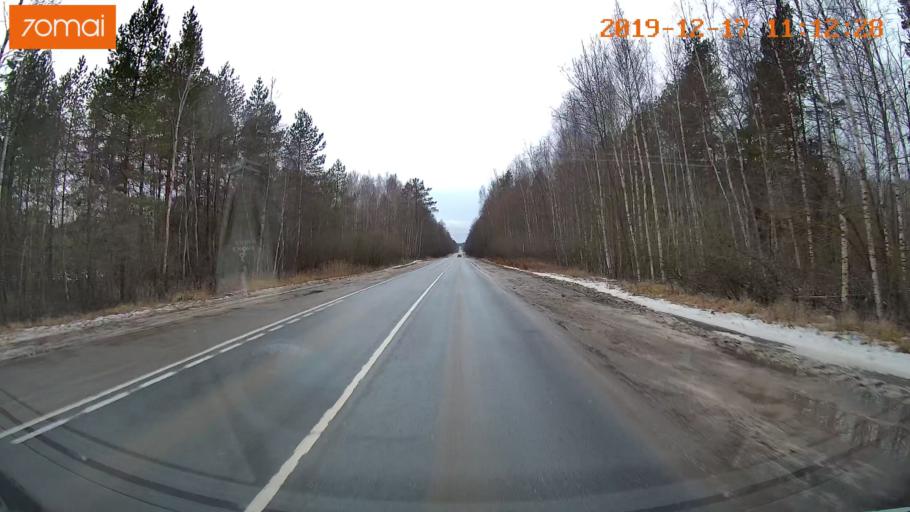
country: RU
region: Vladimir
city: Gus'-Khrustal'nyy
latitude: 55.5753
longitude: 40.6281
